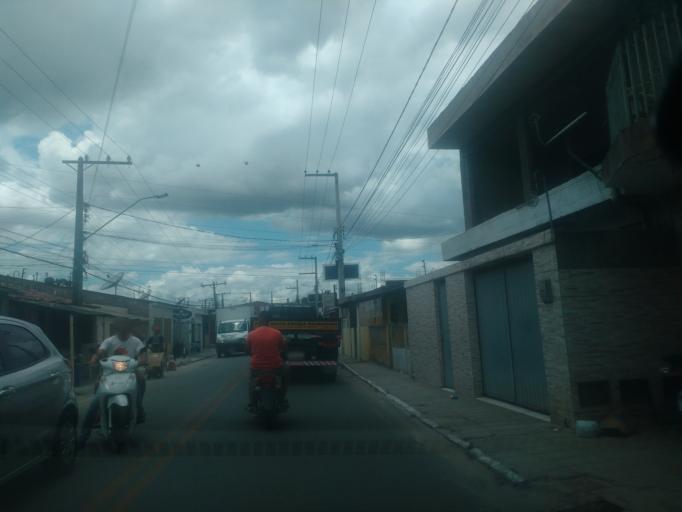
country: BR
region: Alagoas
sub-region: Uniao Dos Palmares
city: Uniao dos Palmares
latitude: -9.1548
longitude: -36.0239
